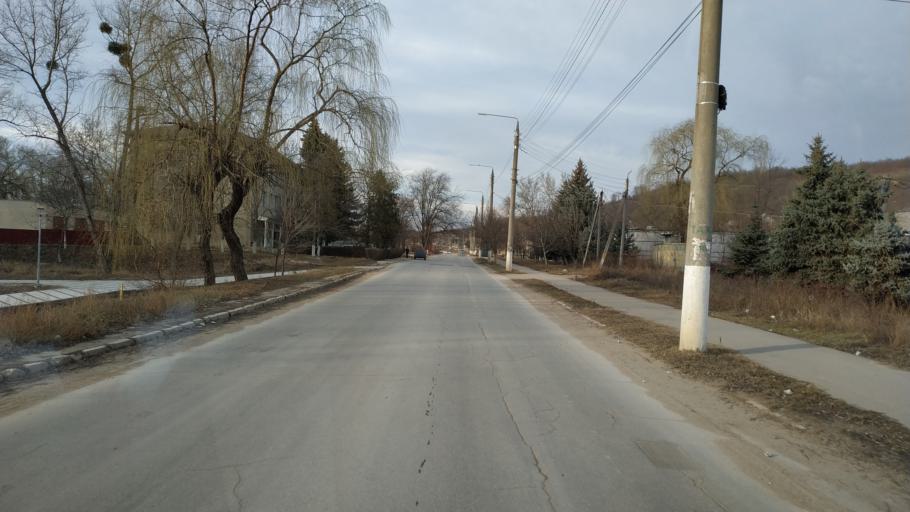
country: MD
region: Nisporeni
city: Nisporeni
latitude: 47.0846
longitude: 28.1824
